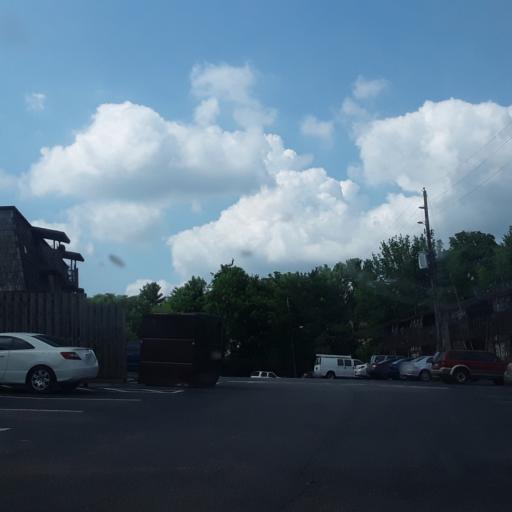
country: US
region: Tennessee
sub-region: Davidson County
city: Oak Hill
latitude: 36.1142
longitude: -86.7352
